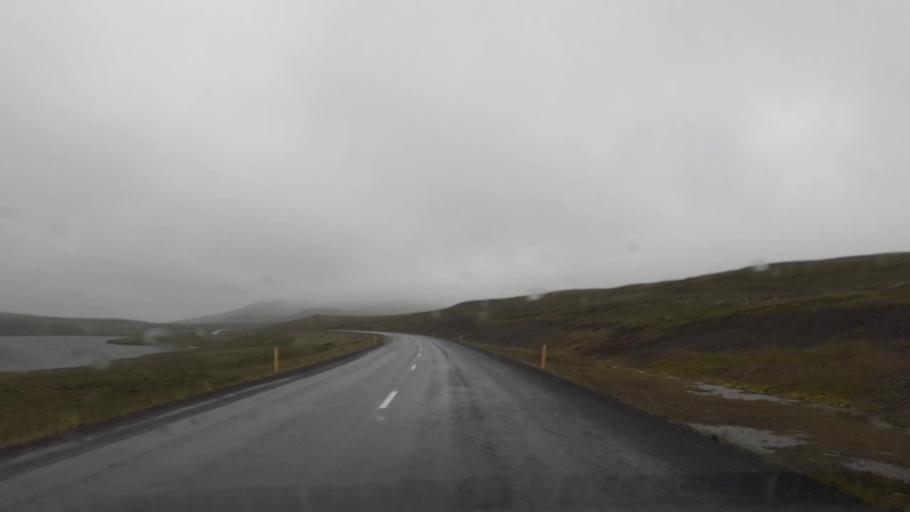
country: IS
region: Northeast
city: Husavik
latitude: 66.2456
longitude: -15.8163
